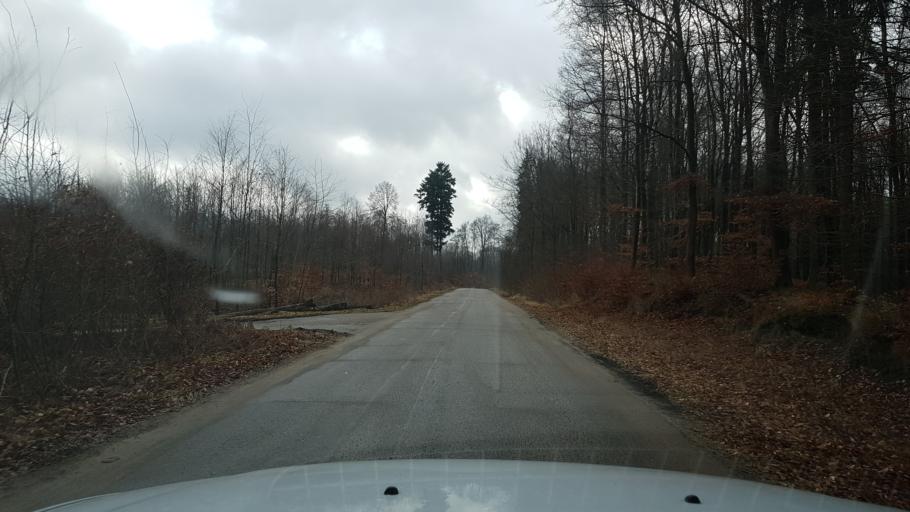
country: PL
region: West Pomeranian Voivodeship
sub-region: Powiat szczecinecki
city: Szczecinek
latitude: 53.6994
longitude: 16.7664
